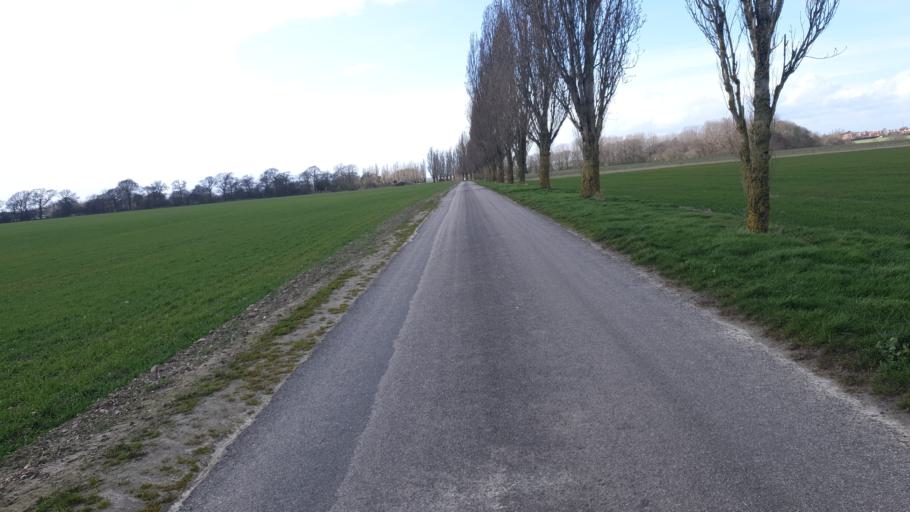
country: GB
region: England
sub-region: Essex
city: Little Clacton
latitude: 51.8501
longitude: 1.1368
